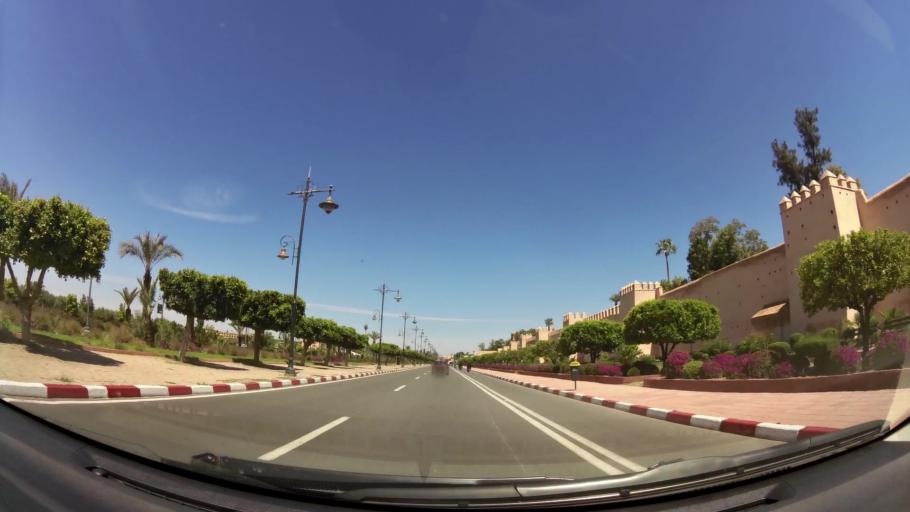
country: MA
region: Marrakech-Tensift-Al Haouz
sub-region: Marrakech
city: Marrakesh
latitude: 31.6187
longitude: -7.9975
